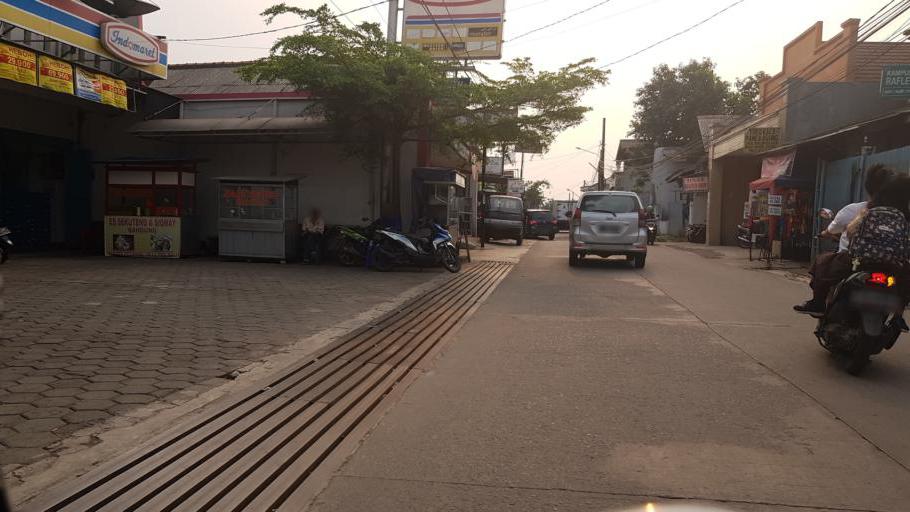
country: ID
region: West Java
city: Depok
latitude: -6.3723
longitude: 106.8517
